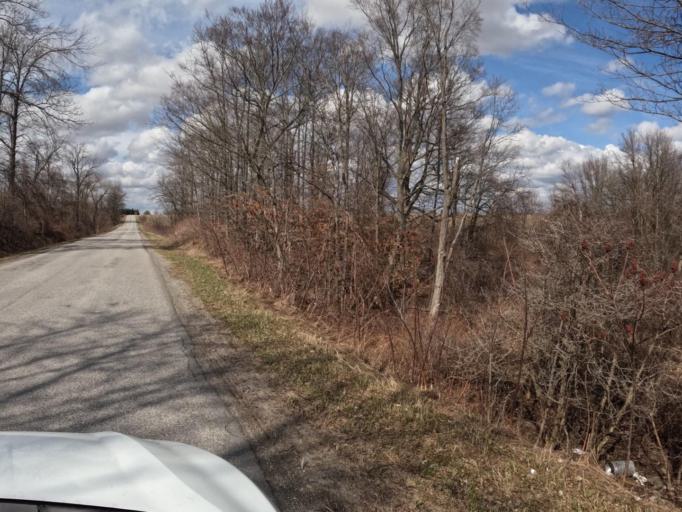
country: CA
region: Ontario
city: Norfolk County
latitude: 42.8953
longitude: -80.1879
